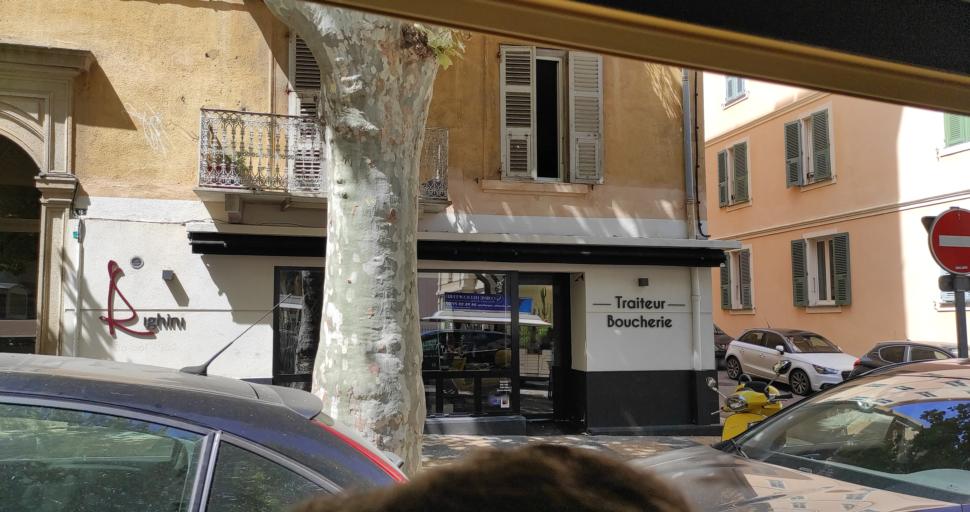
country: FR
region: Corsica
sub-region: Departement de la Corse-du-Sud
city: Ajaccio
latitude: 41.9175
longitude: 8.7302
